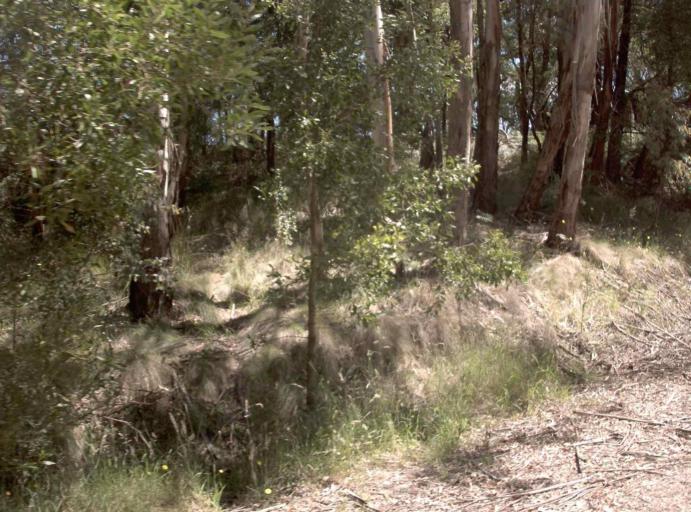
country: AU
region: Victoria
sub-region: East Gippsland
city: Lakes Entrance
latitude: -37.2164
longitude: 148.2672
